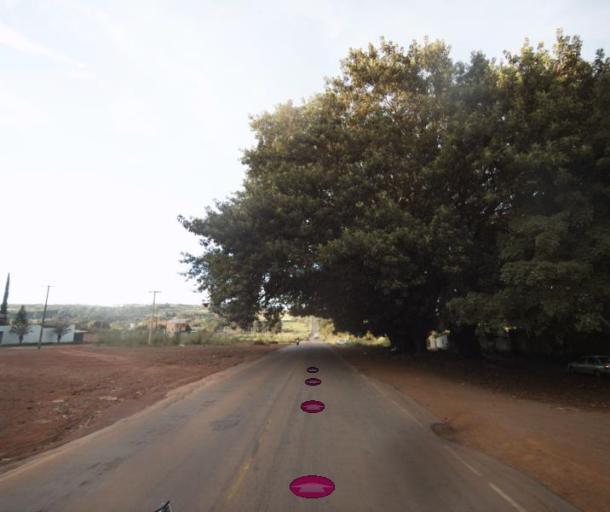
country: BR
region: Goias
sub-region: Anapolis
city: Anapolis
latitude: -16.2784
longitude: -48.9418
